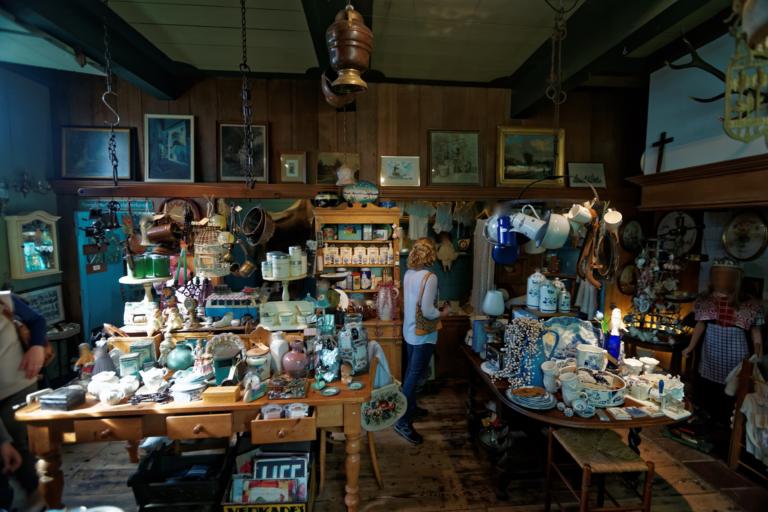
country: NL
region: North Holland
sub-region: Gemeente Zaanstad
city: Zaanstad
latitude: 52.4732
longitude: 4.8172
